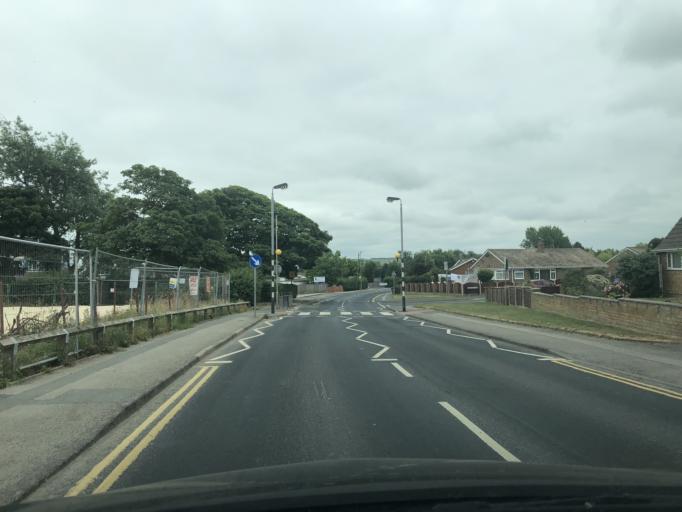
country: GB
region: England
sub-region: North Yorkshire
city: Scarborough
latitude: 54.2394
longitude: -0.3957
